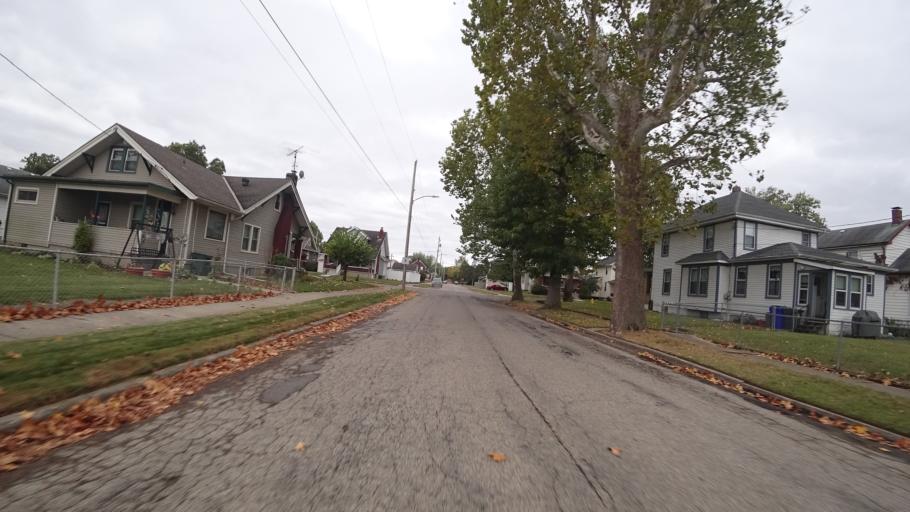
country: US
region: Ohio
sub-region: Butler County
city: Fairfield
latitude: 39.3664
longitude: -84.5607
